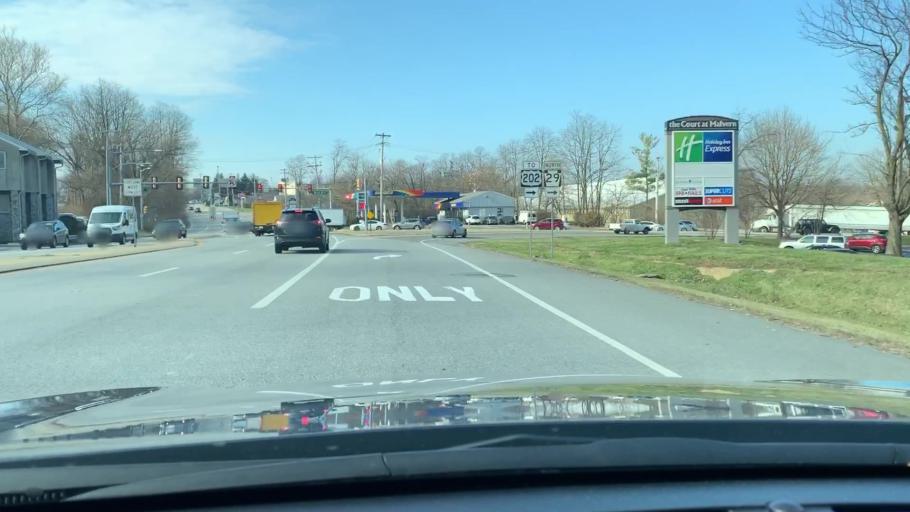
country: US
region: Pennsylvania
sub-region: Chester County
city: Malvern
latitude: 40.0439
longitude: -75.5225
